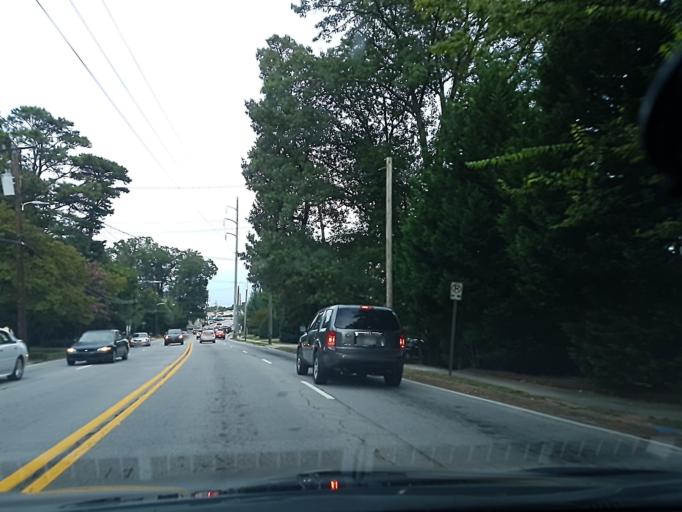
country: US
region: Georgia
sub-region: DeKalb County
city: North Decatur
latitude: 33.7912
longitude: -84.3097
